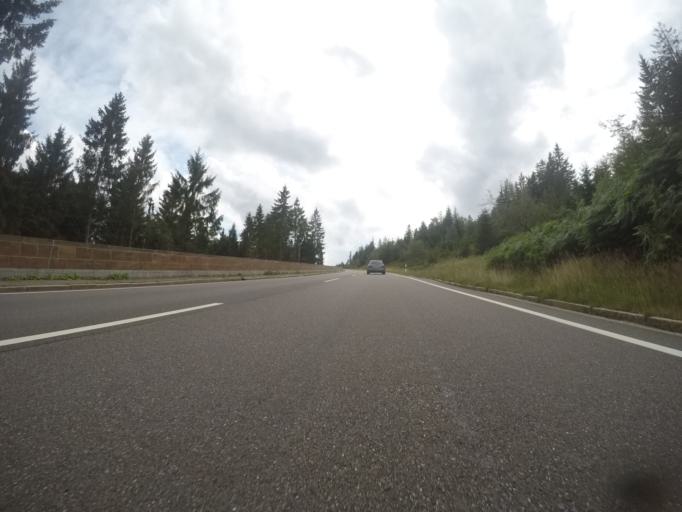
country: DE
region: Baden-Wuerttemberg
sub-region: Freiburg Region
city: Seebach
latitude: 48.5558
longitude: 8.2176
